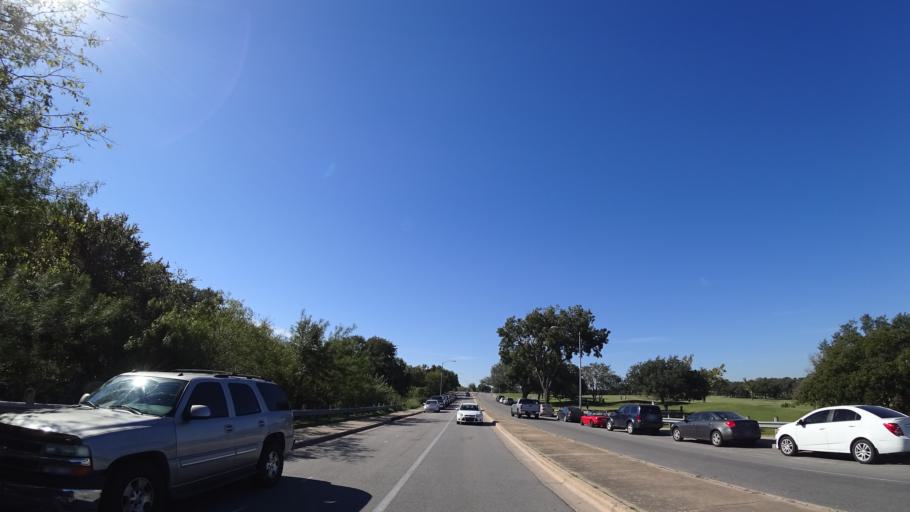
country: US
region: Texas
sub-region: Travis County
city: Austin
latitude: 30.2344
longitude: -97.7047
